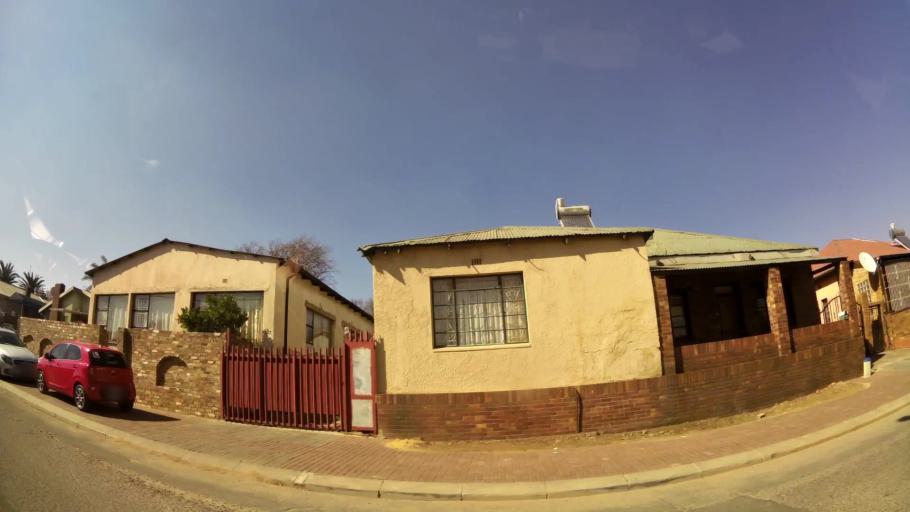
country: ZA
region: Gauteng
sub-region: City of Johannesburg Metropolitan Municipality
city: Johannesburg
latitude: -26.1863
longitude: 27.9662
